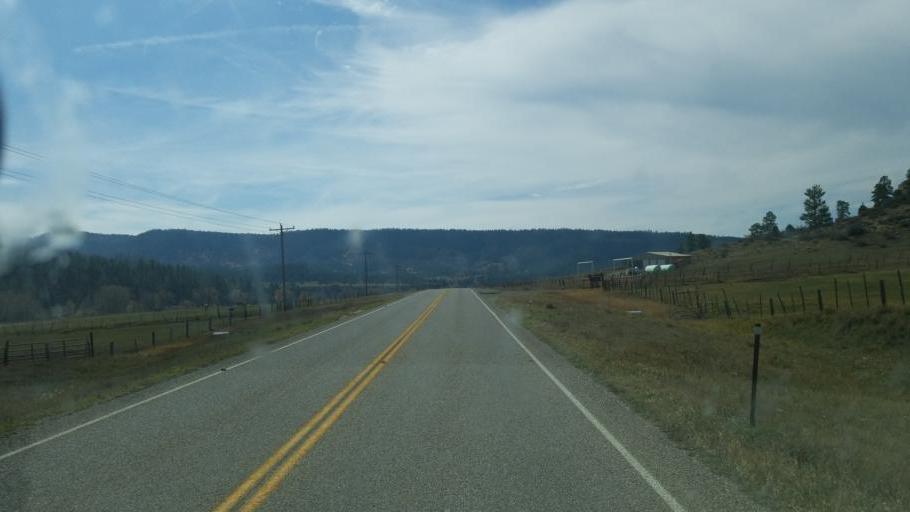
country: US
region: New Mexico
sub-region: Rio Arriba County
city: Dulce
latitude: 37.0486
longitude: -106.8413
